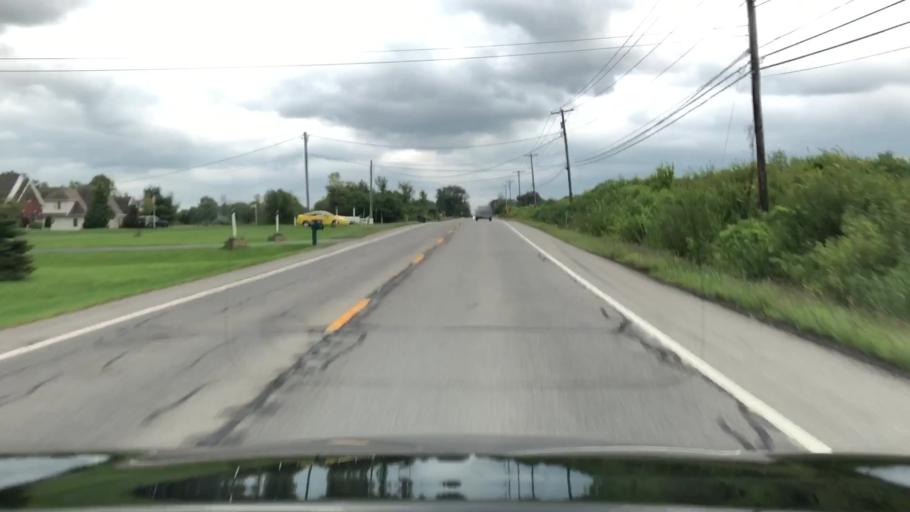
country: US
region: New York
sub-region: Erie County
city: Orchard Park
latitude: 42.7938
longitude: -78.6969
